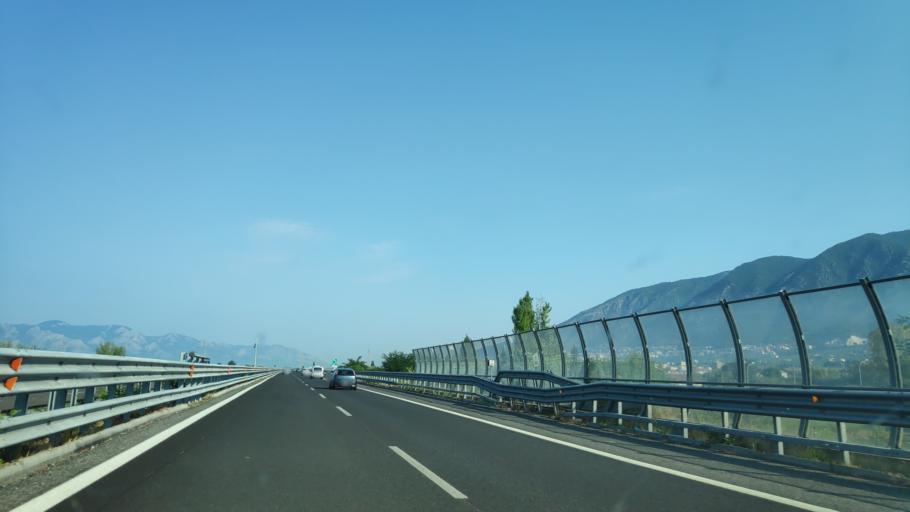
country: IT
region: Campania
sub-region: Provincia di Salerno
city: Sala Consilina
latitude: 40.3635
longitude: 15.6067
